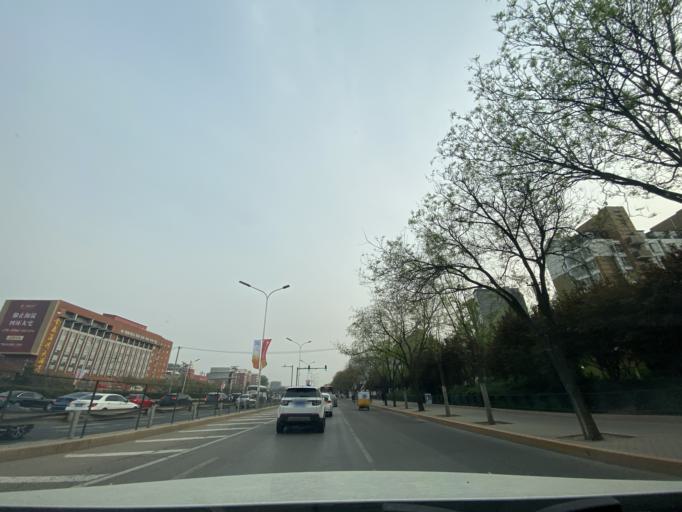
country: CN
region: Beijing
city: Sijiqing
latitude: 39.9379
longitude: 116.2679
